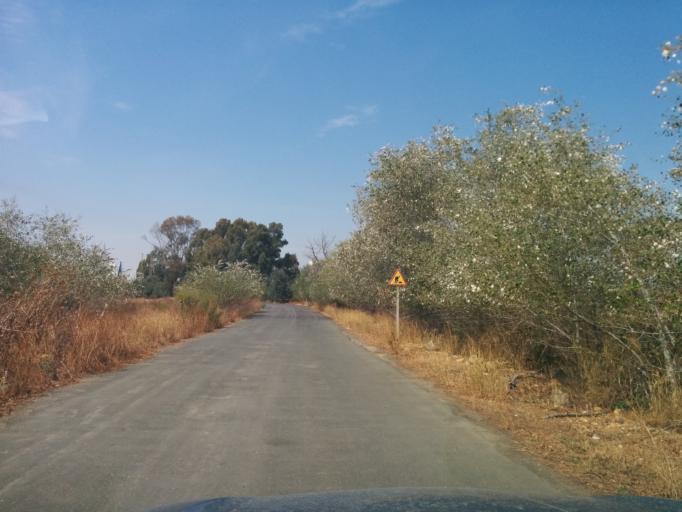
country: ES
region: Andalusia
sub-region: Provincia de Sevilla
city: Gelves
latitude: 37.3168
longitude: -5.9970
